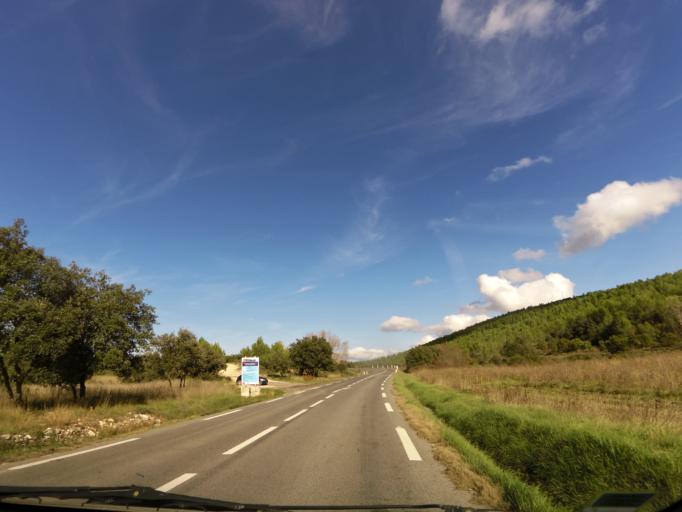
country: FR
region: Languedoc-Roussillon
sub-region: Departement du Gard
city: Villevieille
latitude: 43.8535
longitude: 4.0963
